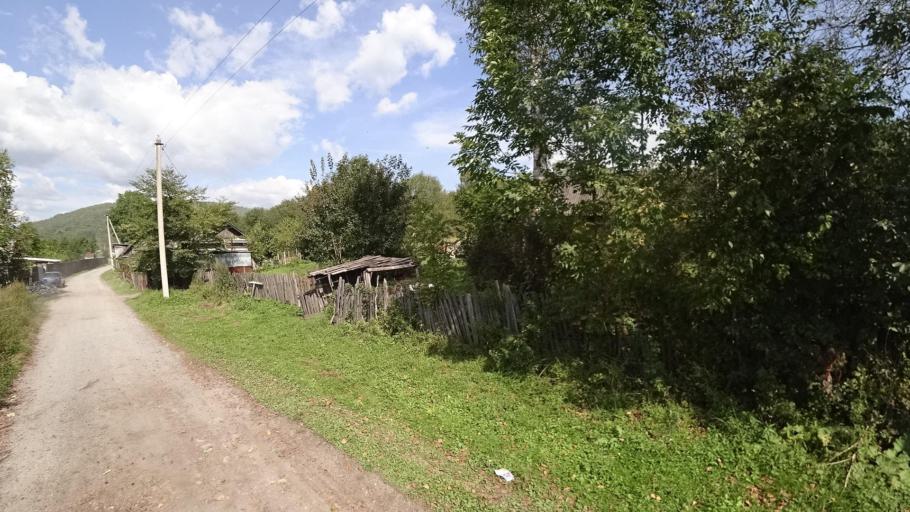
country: RU
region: Jewish Autonomous Oblast
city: Londoko
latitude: 49.0245
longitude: 131.9326
